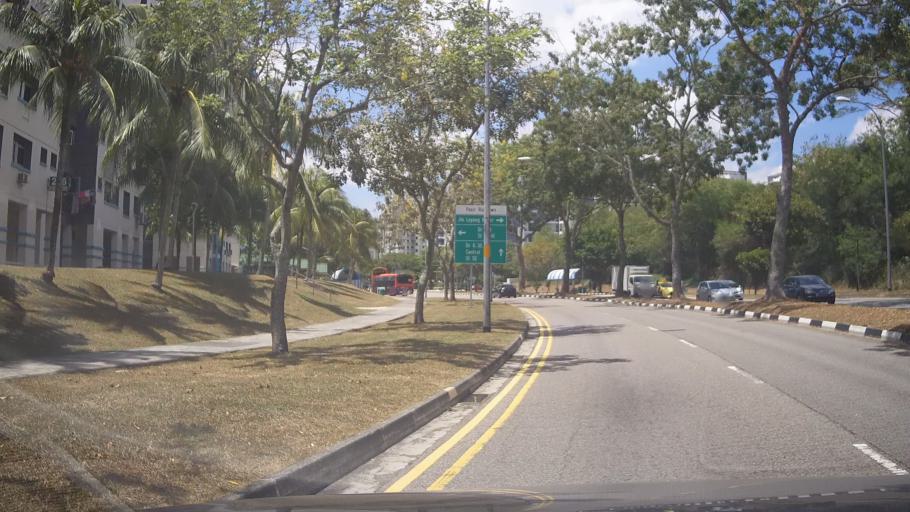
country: MY
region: Johor
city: Kampung Pasir Gudang Baru
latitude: 1.3745
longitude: 103.9631
